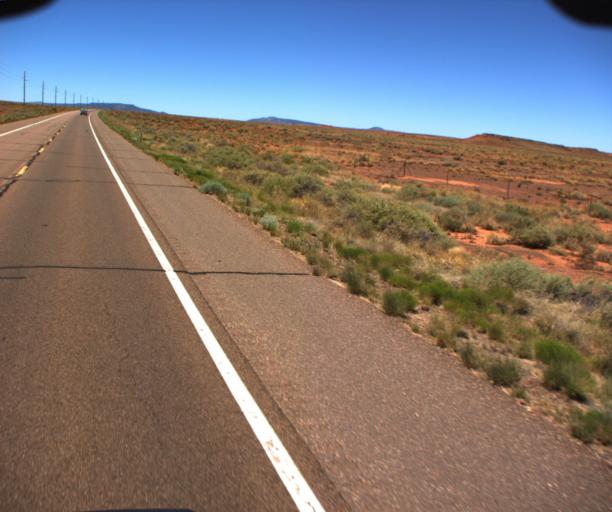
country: US
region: Arizona
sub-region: Navajo County
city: Winslow
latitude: 34.9719
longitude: -110.7279
